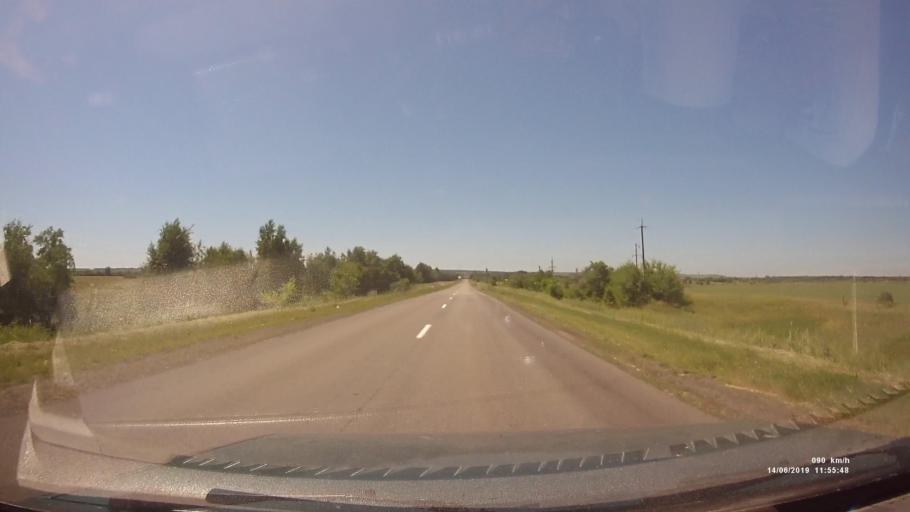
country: RU
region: Rostov
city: Kazanskaya
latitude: 49.8075
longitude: 41.1708
